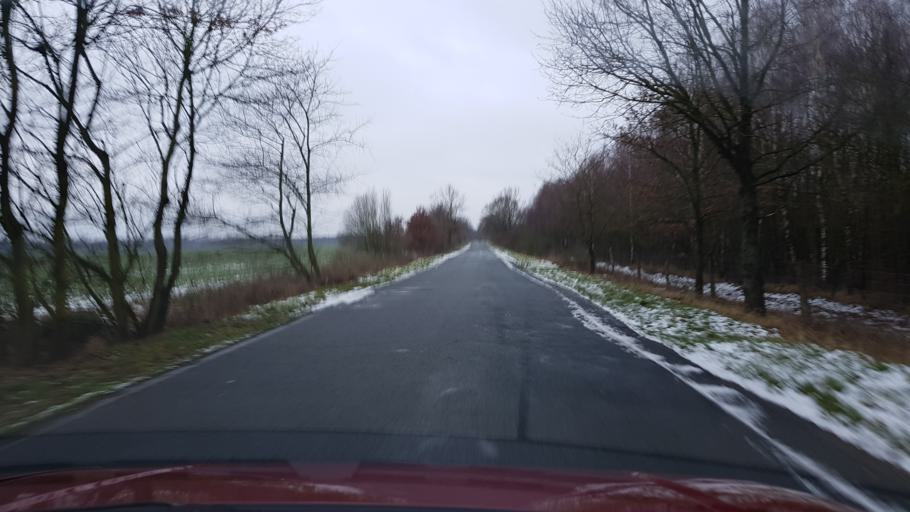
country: PL
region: West Pomeranian Voivodeship
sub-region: Powiat gryficki
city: Ploty
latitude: 53.6866
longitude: 15.2421
